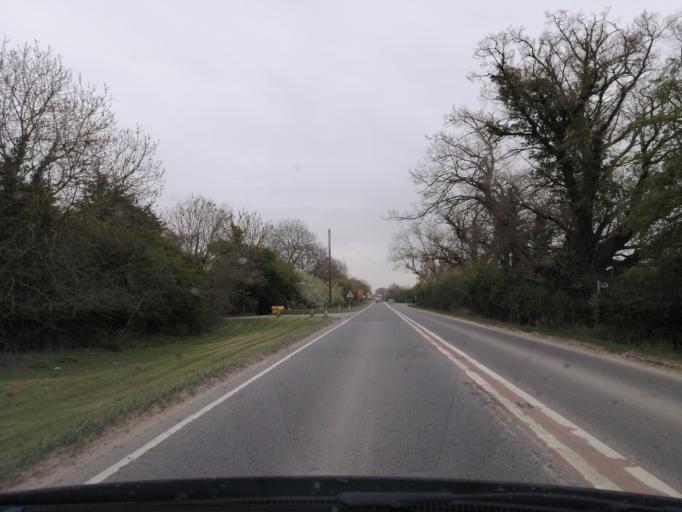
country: GB
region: England
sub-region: Peterborough
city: Wittering
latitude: 52.5908
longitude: -0.4526
